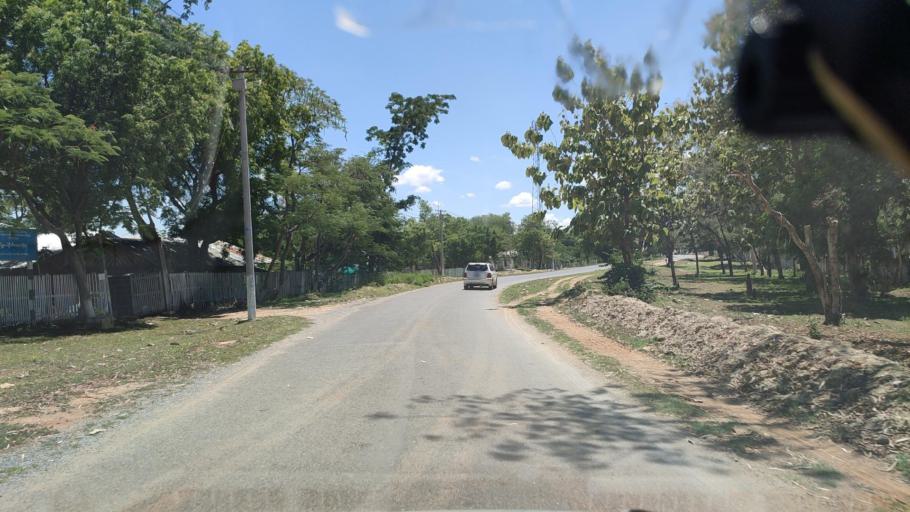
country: MM
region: Magway
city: Myaydo
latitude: 19.7283
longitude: 95.1683
